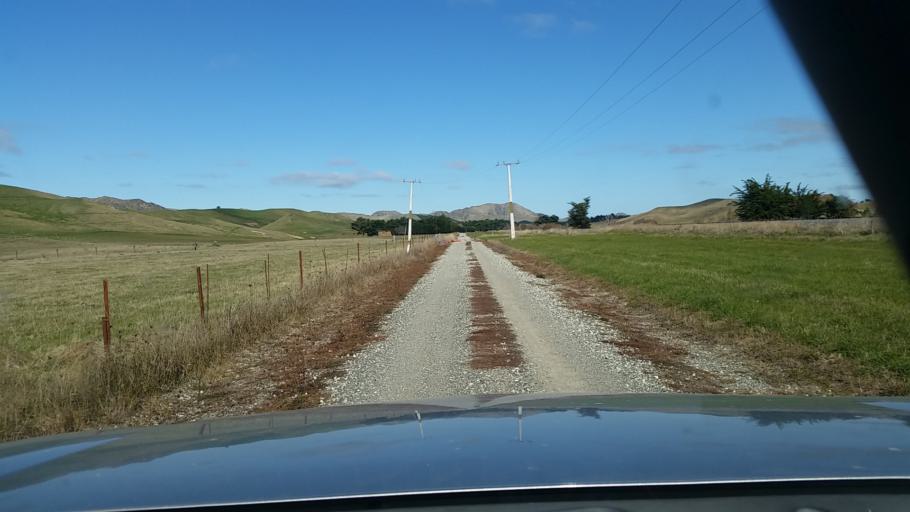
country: NZ
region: Marlborough
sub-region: Marlborough District
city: Blenheim
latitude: -41.7458
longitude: 174.1573
